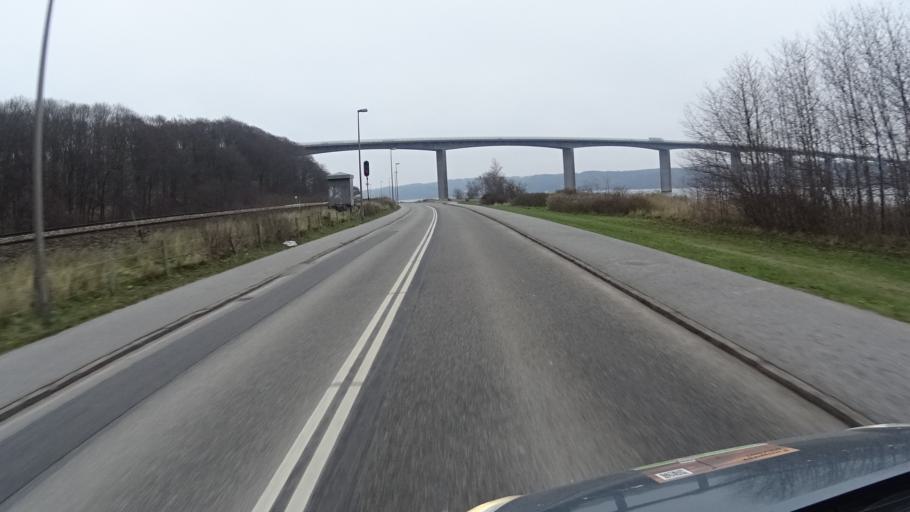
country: DK
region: South Denmark
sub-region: Vejle Kommune
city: Vejle
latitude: 55.7073
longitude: 9.5696
